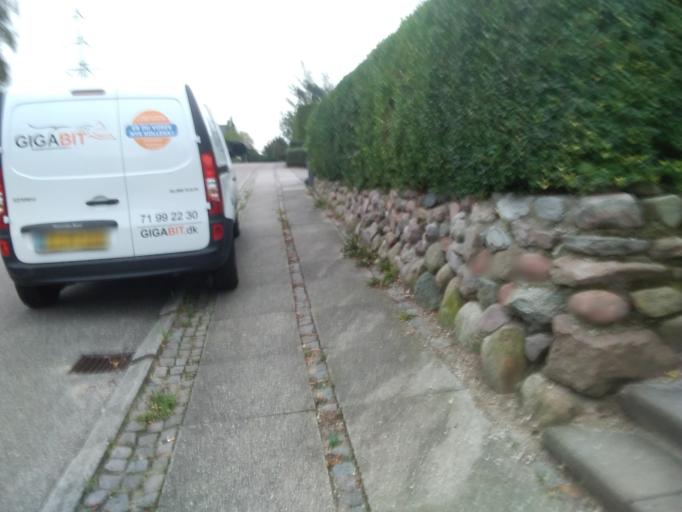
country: DK
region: Capital Region
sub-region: Egedal Kommune
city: Stenlose
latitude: 55.7722
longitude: 12.2086
